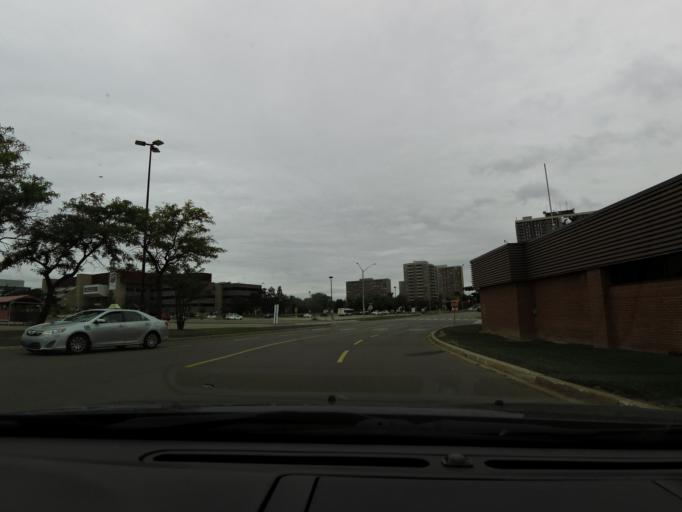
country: CA
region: Ontario
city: Brampton
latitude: 43.7164
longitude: -79.7188
